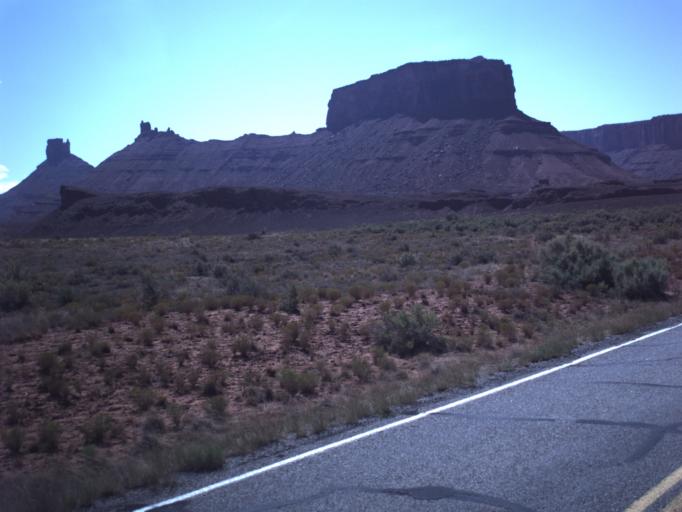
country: US
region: Utah
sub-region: Grand County
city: Moab
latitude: 38.7097
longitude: -109.3776
